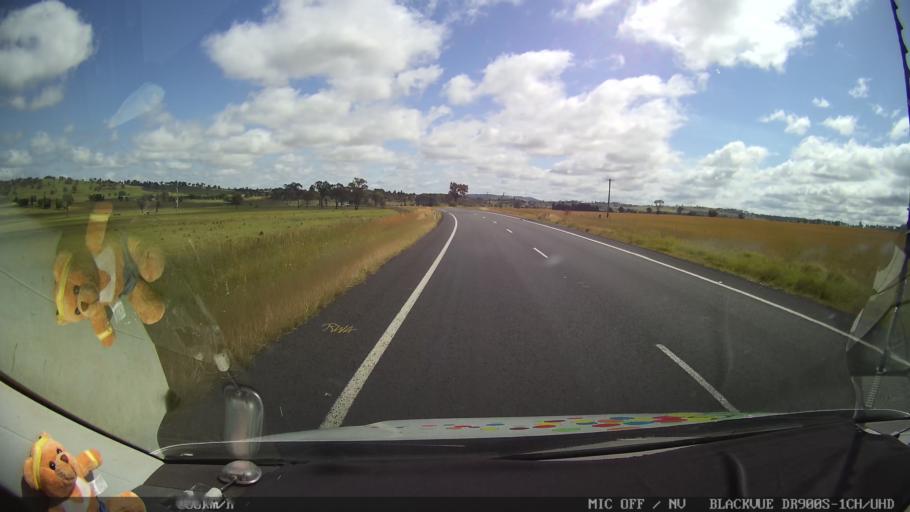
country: AU
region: New South Wales
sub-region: Glen Innes Severn
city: Glen Innes
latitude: -29.9424
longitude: 151.7224
